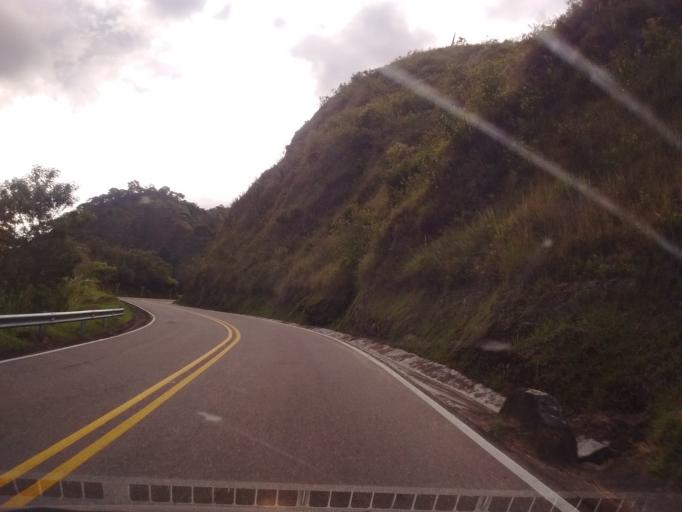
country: CO
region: Huila
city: San Agustin
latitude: 1.8720
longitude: -76.2360
